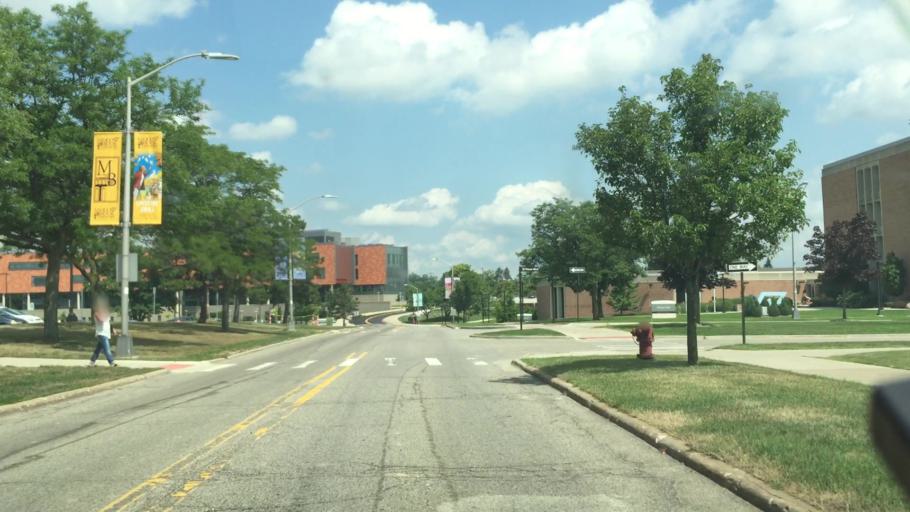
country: US
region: Michigan
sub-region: Oakland County
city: Auburn Hills
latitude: 42.6748
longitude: -83.2185
